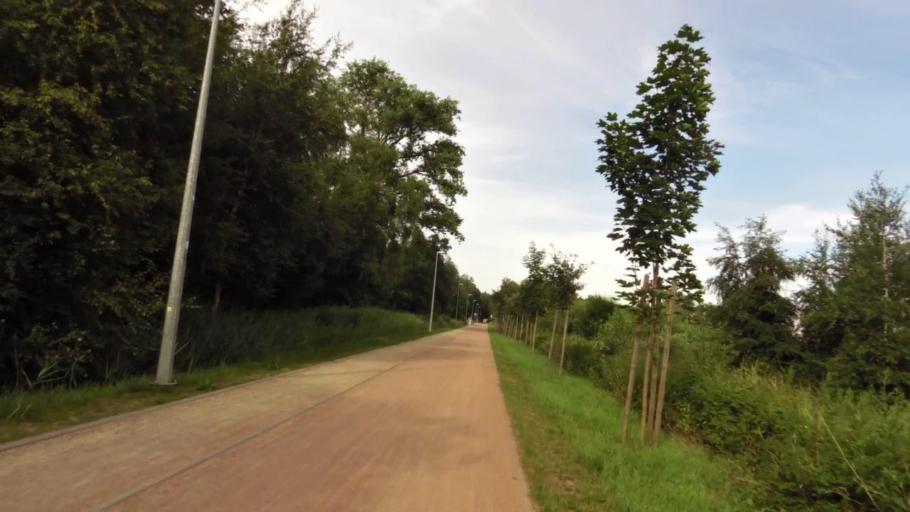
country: PL
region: West Pomeranian Voivodeship
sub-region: Powiat kolobrzeski
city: Grzybowo
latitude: 54.1727
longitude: 15.5257
